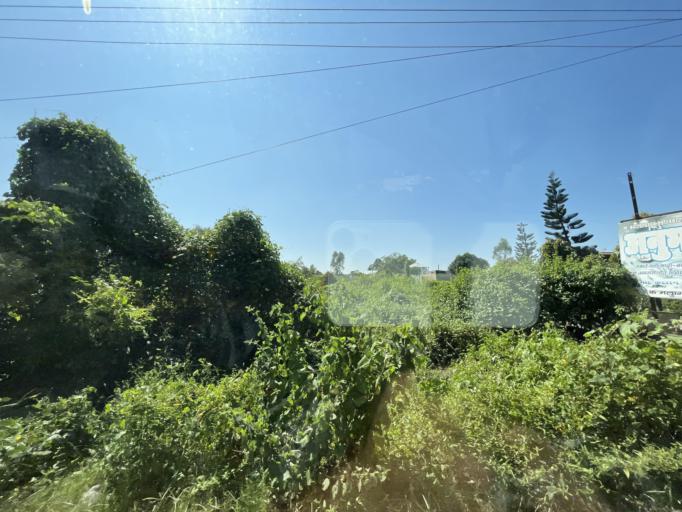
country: IN
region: Uttarakhand
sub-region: Naini Tal
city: Haldwani
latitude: 29.2108
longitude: 79.4629
